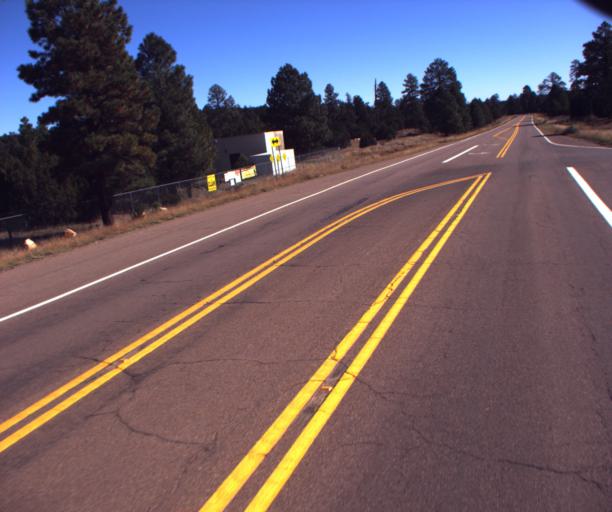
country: US
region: Arizona
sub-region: Navajo County
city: Heber-Overgaard
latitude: 34.4294
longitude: -110.5498
